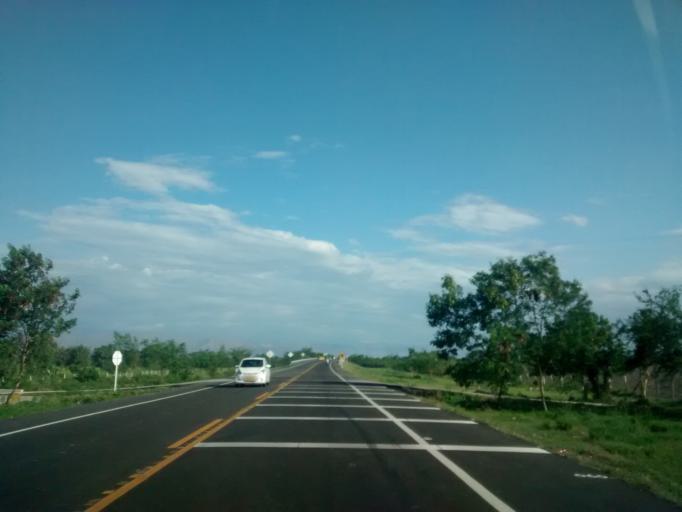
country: CO
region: Tolima
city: Espinal
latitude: 4.1487
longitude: -74.9131
